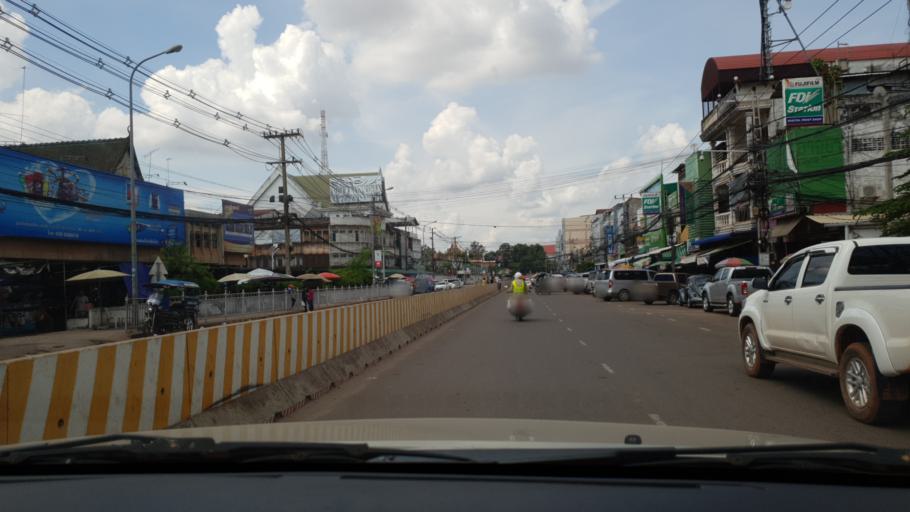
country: LA
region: Vientiane
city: Vientiane
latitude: 17.9641
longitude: 102.6149
